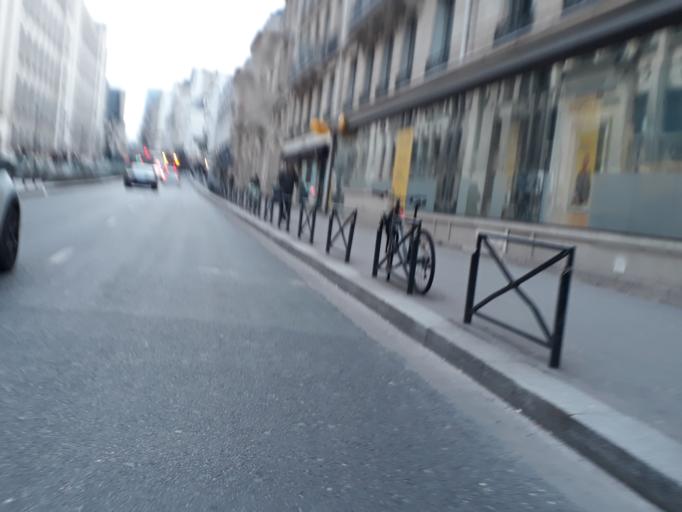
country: FR
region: Ile-de-France
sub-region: Paris
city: Paris
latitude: 48.8563
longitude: 2.3318
